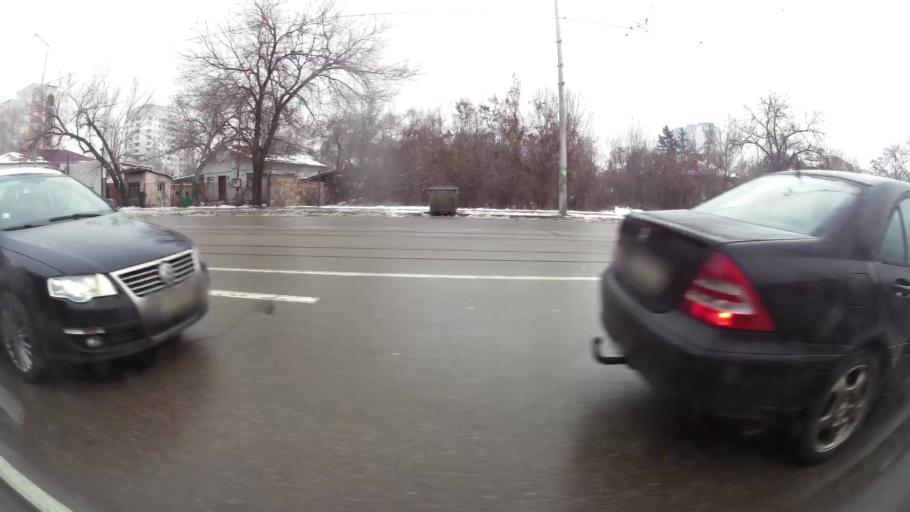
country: BG
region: Sofia-Capital
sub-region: Stolichna Obshtina
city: Sofia
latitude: 42.7080
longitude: 23.2993
